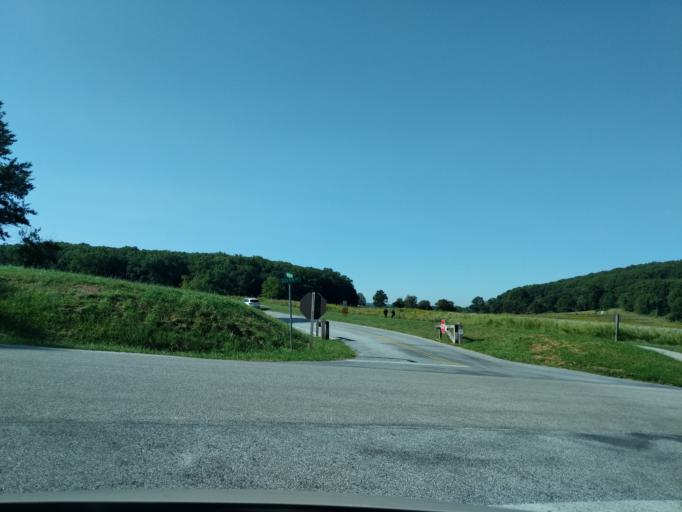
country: US
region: Pennsylvania
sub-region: Chester County
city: Chesterbrook
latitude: 40.0927
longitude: -75.4393
